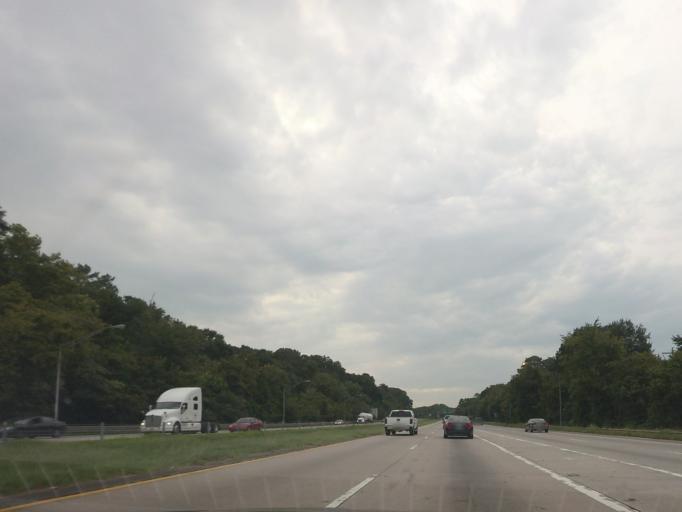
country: US
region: Georgia
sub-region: Bibb County
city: Macon
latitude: 32.8502
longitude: -83.6295
